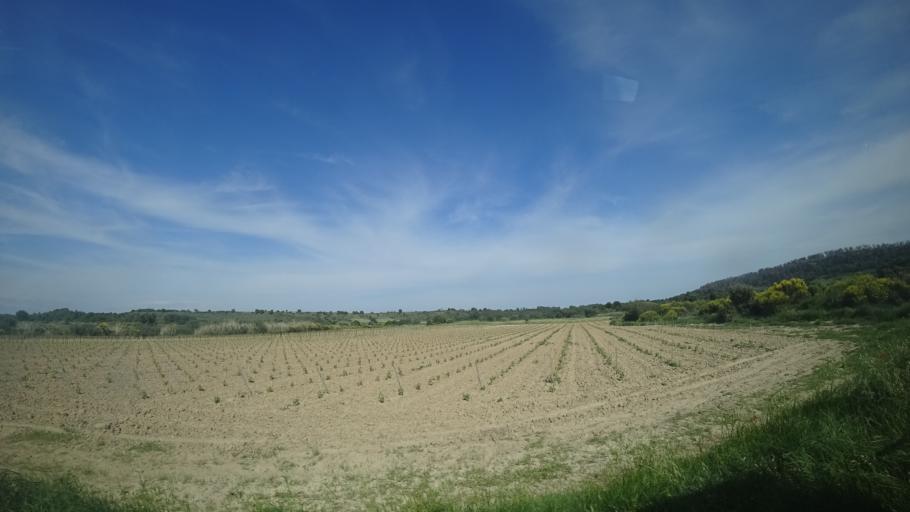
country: FR
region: Languedoc-Roussillon
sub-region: Departement de l'Aude
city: Canet
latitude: 43.2704
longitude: 2.8144
